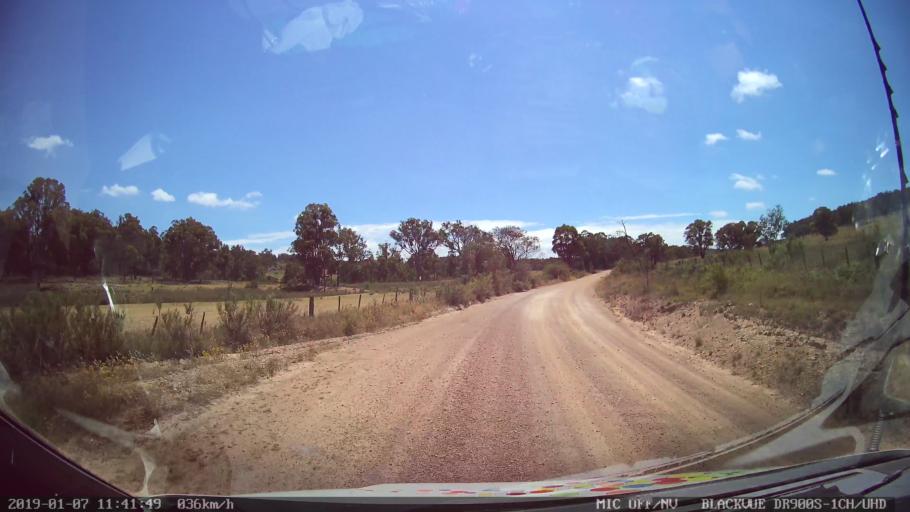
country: AU
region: New South Wales
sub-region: Guyra
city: Guyra
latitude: -30.3587
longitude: 151.5901
